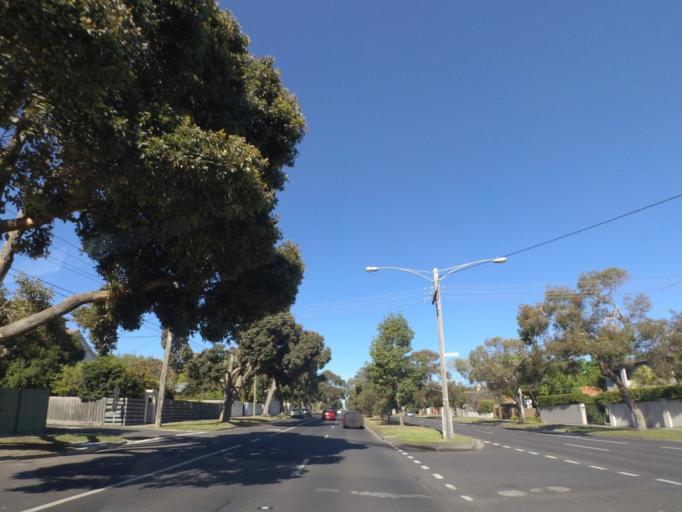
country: AU
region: Victoria
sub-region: Bayside
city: Hampton
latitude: -37.9283
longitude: 144.9963
